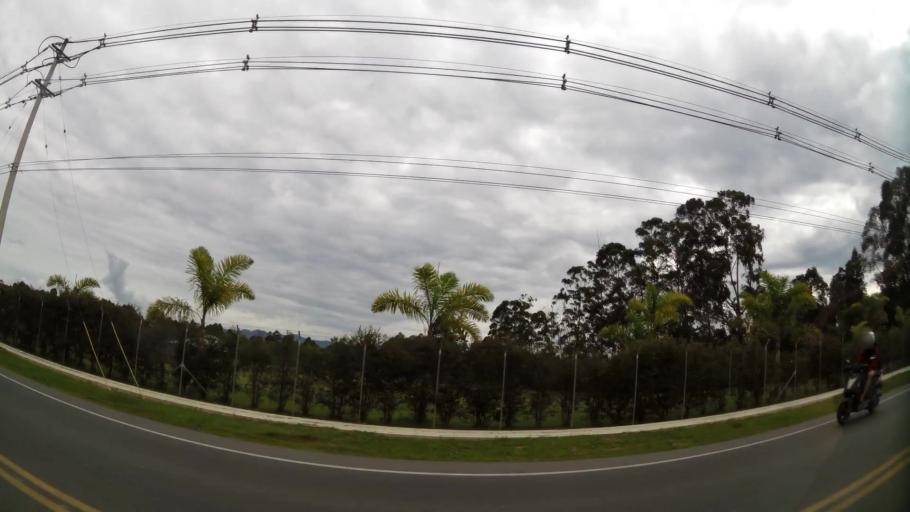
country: CO
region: Antioquia
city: Rionegro
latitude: 6.1452
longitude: -75.4293
